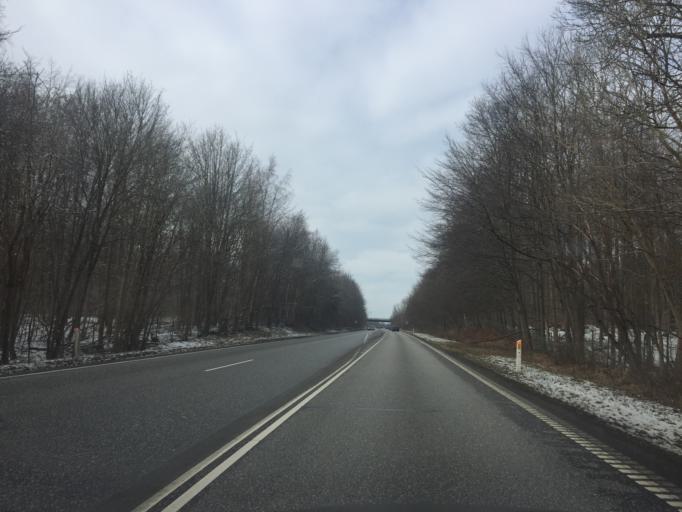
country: DK
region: Capital Region
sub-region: Hillerod Kommune
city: Hillerod
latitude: 55.8864
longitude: 12.2973
